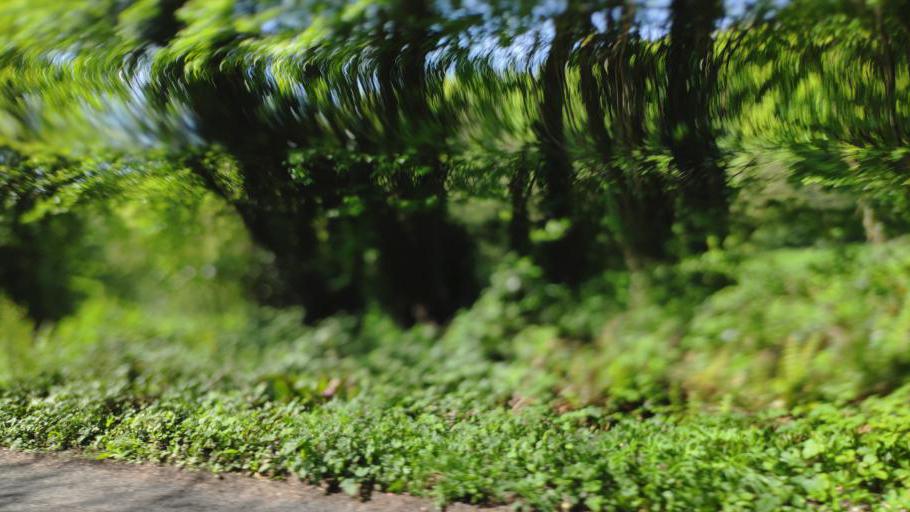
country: IE
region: Munster
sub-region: County Cork
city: Blarney
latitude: 51.9703
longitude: -8.5788
